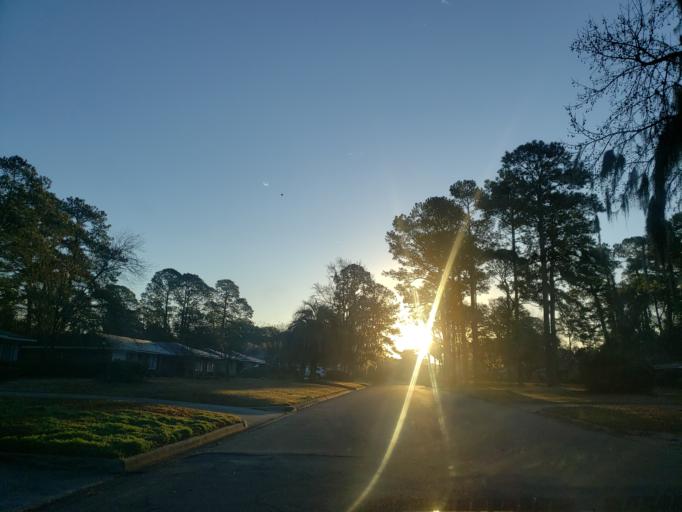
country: US
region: Georgia
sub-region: Chatham County
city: Thunderbolt
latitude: 32.0167
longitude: -81.0830
